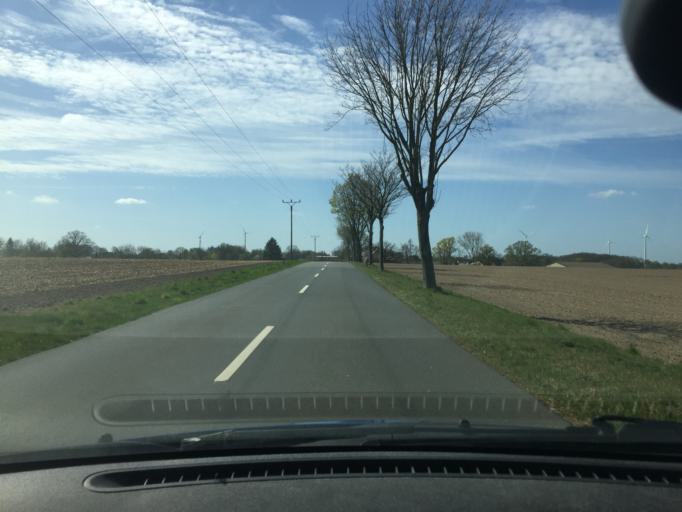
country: DE
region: Lower Saxony
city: Ratzlingen
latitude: 52.9650
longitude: 10.6730
